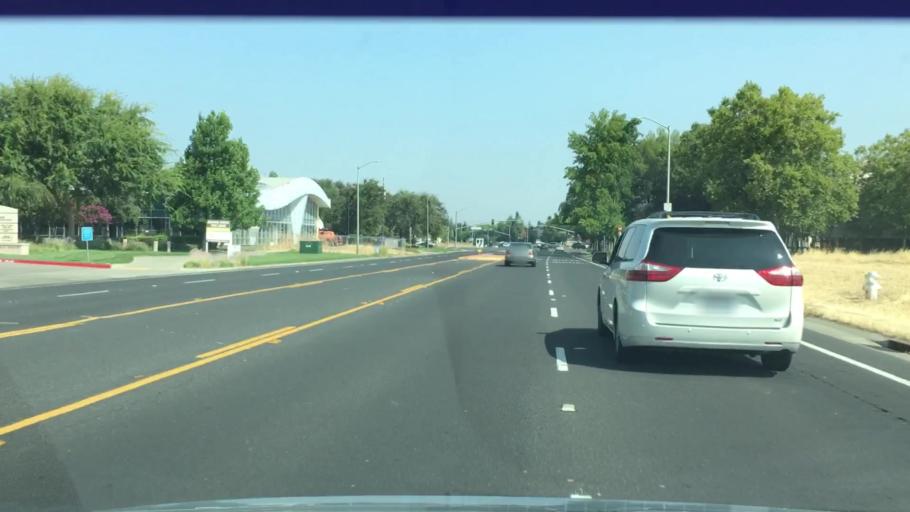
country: US
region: California
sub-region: Sacramento County
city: Laguna
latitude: 38.4196
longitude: -121.4063
